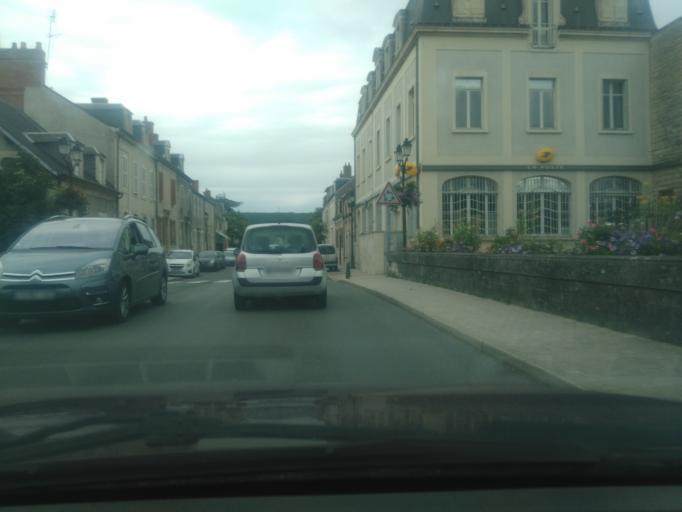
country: FR
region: Centre
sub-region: Departement du Cher
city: Saint-Amand-Montrond
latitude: 46.7241
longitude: 2.5059
